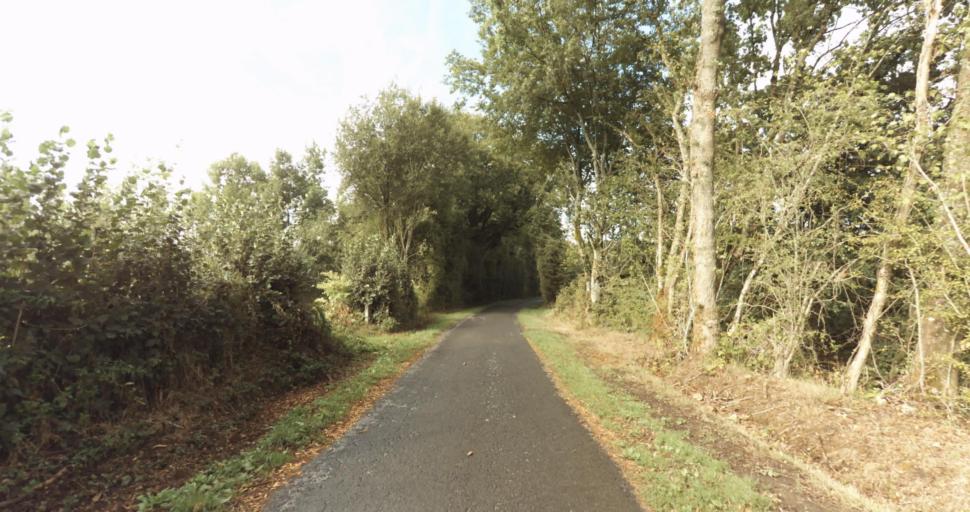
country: FR
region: Lower Normandy
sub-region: Departement de l'Orne
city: Sainte-Gauburge-Sainte-Colombe
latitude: 48.6701
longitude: 0.3820
